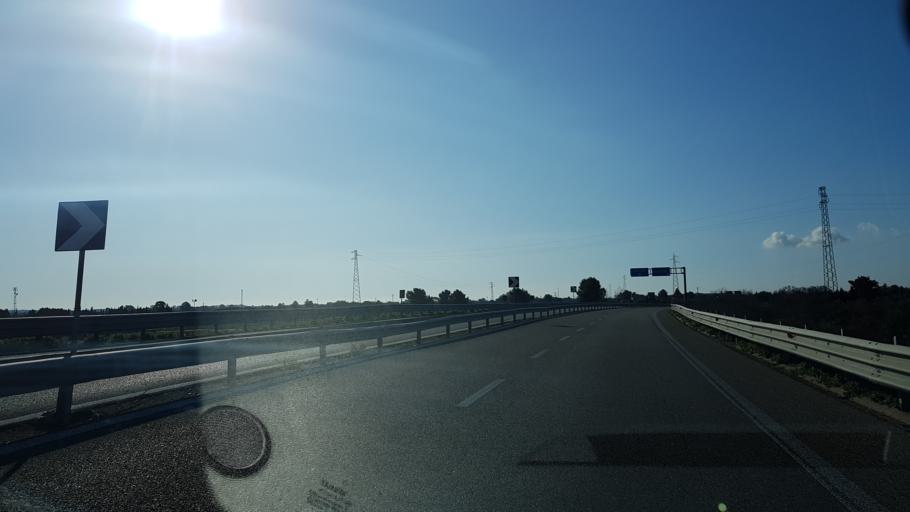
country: IT
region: Apulia
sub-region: Provincia di Lecce
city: Galatone
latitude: 40.1277
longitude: 18.0531
